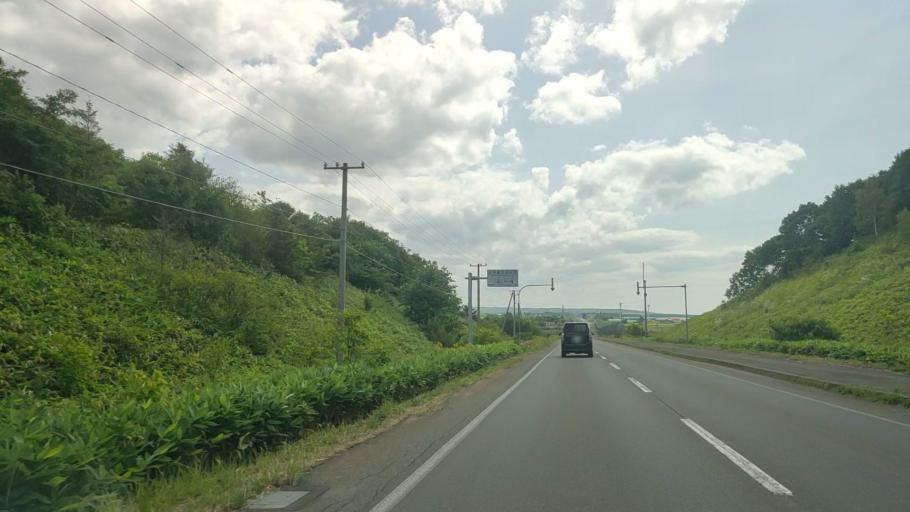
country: JP
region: Hokkaido
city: Makubetsu
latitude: 44.7625
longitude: 141.7938
